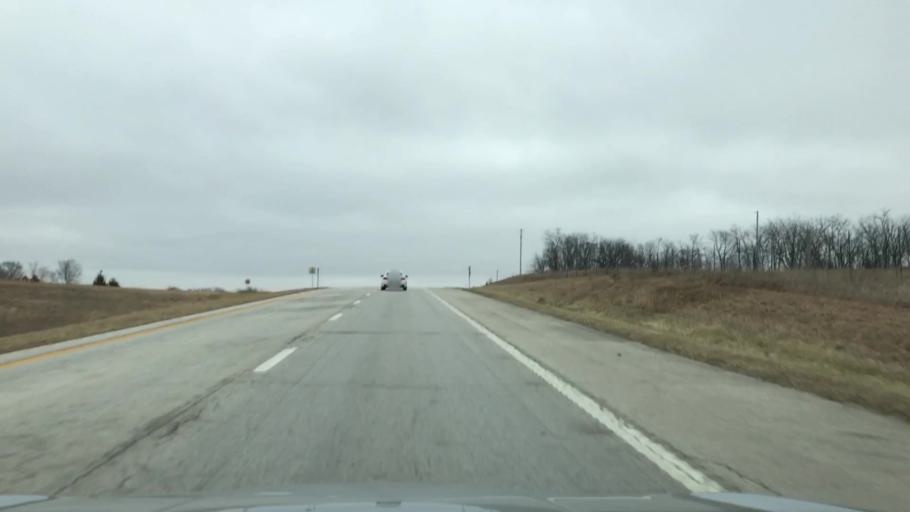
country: US
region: Missouri
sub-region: Linn County
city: Marceline
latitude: 39.7590
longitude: -92.8722
